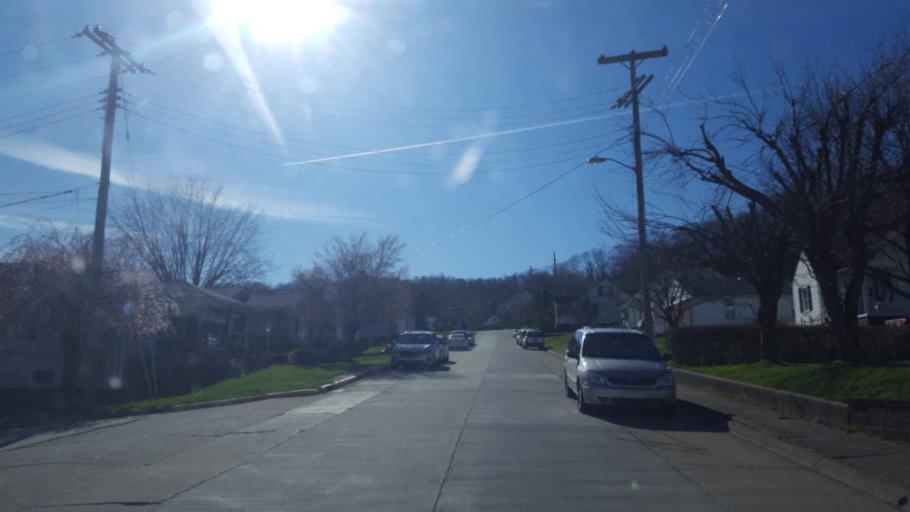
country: US
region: Ohio
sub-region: Jefferson County
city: Toronto
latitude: 40.4549
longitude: -80.6118
